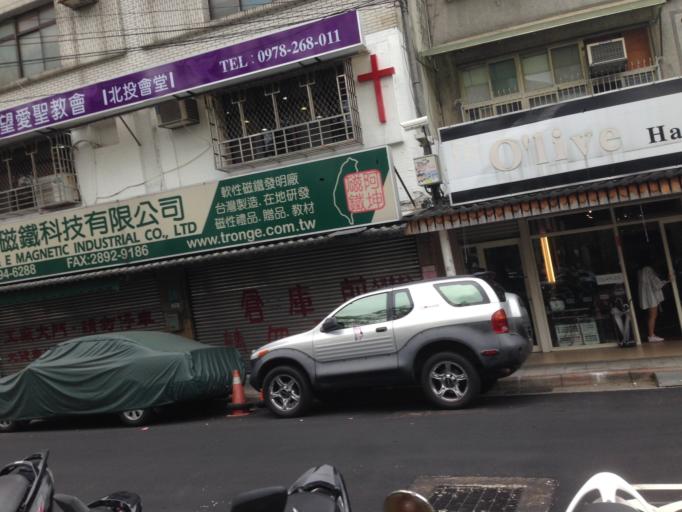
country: TW
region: Taipei
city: Taipei
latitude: 25.1329
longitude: 121.4984
